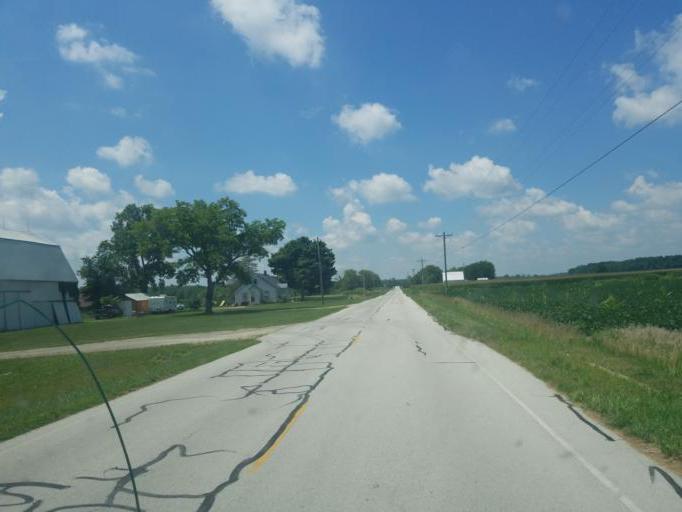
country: US
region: Ohio
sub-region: Allen County
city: Spencerville
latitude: 40.6771
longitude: -84.4924
